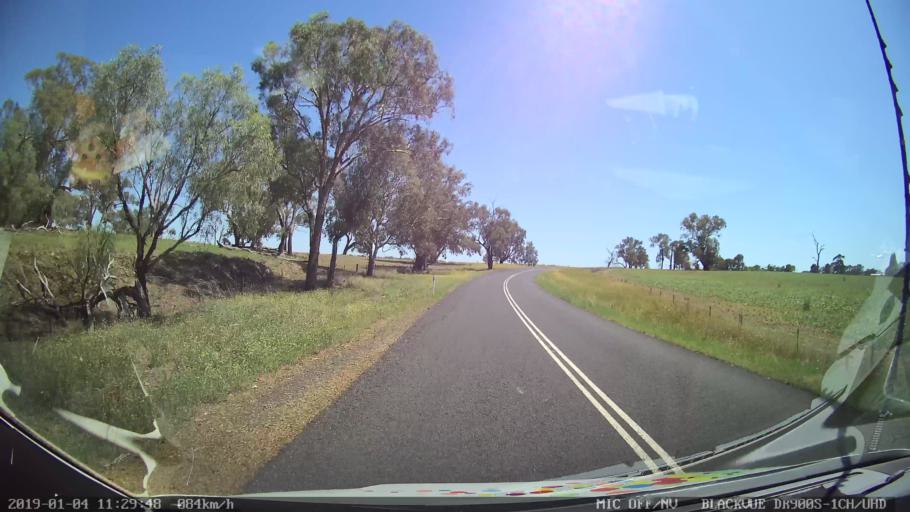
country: AU
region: New South Wales
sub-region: Cabonne
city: Molong
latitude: -33.0837
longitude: 148.7760
